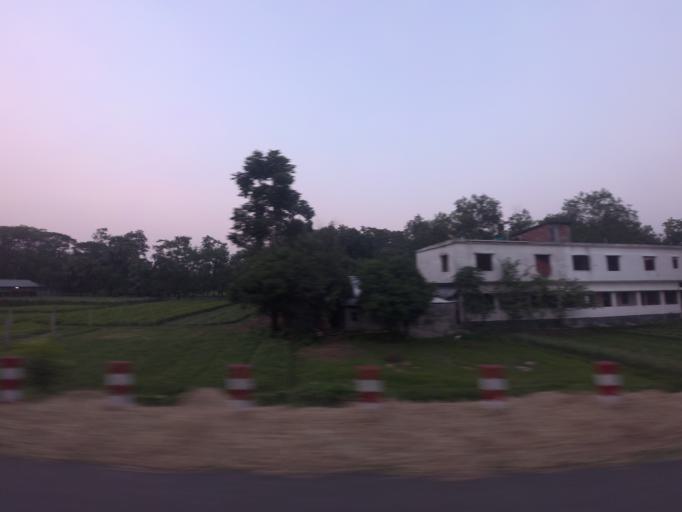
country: BD
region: Chittagong
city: Comilla
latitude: 23.4794
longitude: 91.0686
